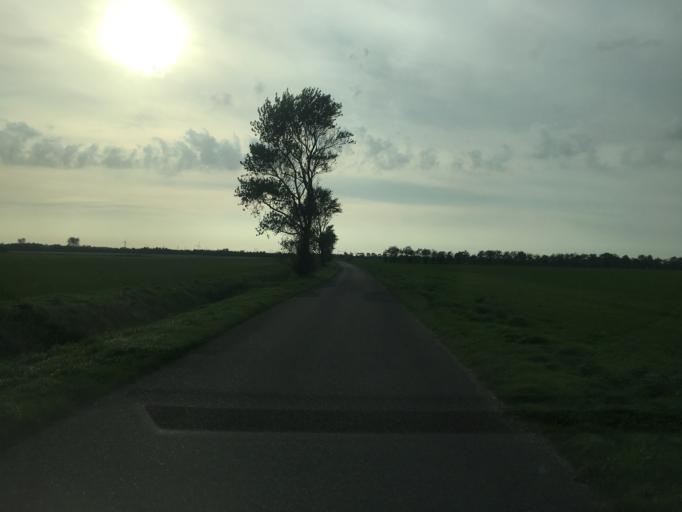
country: DE
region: Schleswig-Holstein
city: Bramstedtlund
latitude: 54.9138
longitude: 9.0610
